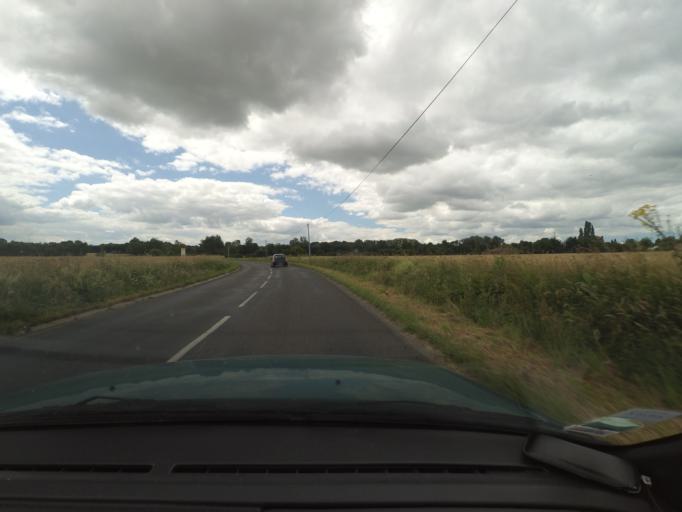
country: FR
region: Pays de la Loire
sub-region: Departement de la Loire-Atlantique
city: Saint-Hilaire-de-Clisson
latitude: 47.0410
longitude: -1.3250
